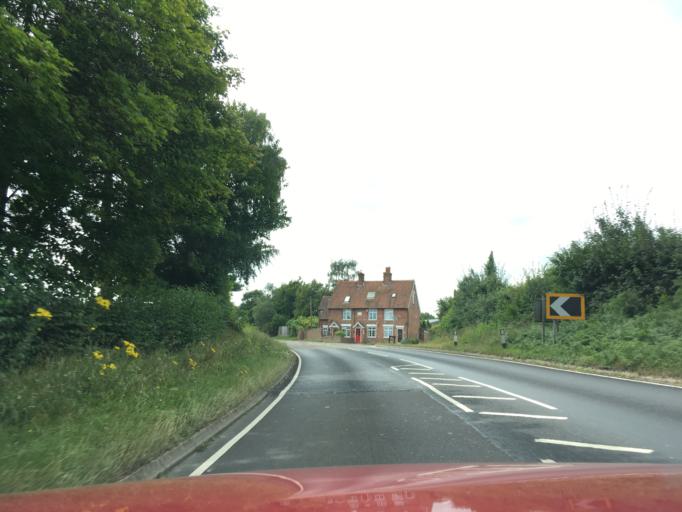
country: GB
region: England
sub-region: Kent
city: Cranbrook
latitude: 51.1139
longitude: 0.5257
